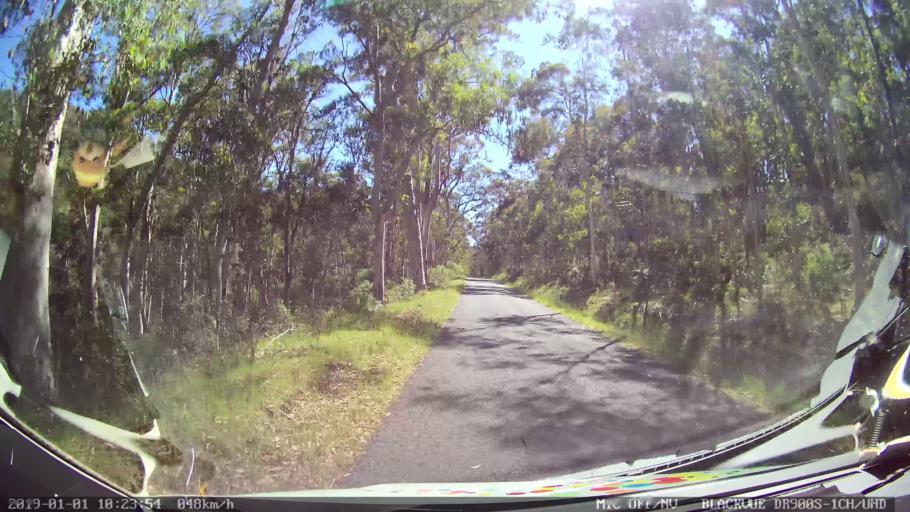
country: AU
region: New South Wales
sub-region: Snowy River
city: Jindabyne
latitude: -36.0744
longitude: 148.2155
